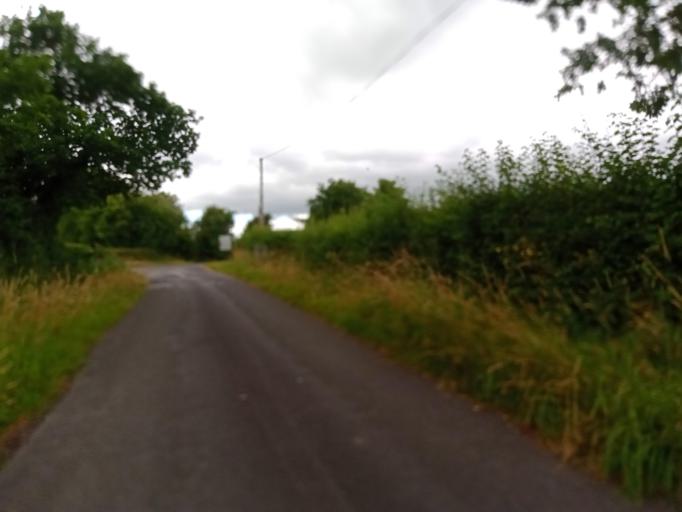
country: IE
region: Leinster
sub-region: Kilkenny
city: Callan
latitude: 52.5738
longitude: -7.4065
